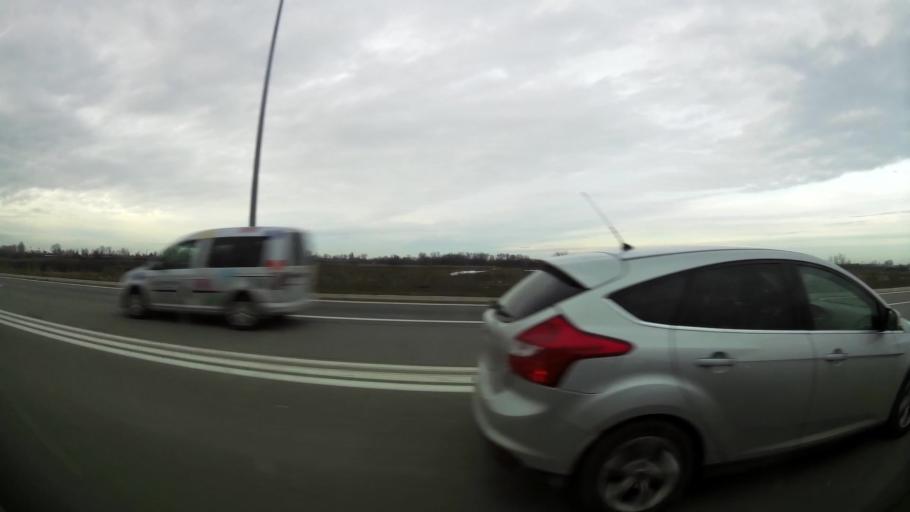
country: RS
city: Ostruznica
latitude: 44.7381
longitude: 20.3414
